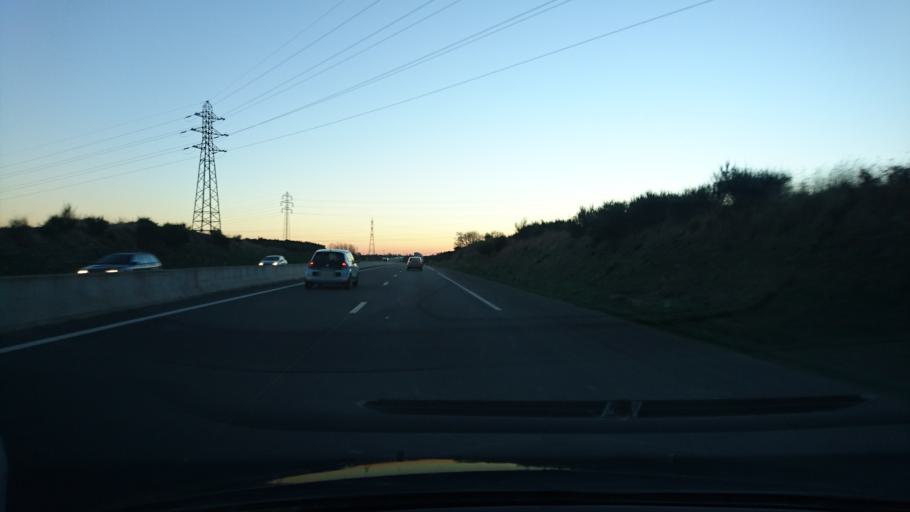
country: FR
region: Brittany
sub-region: Departement des Cotes-d'Armor
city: Ploufragan
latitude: 48.4791
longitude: -2.7824
